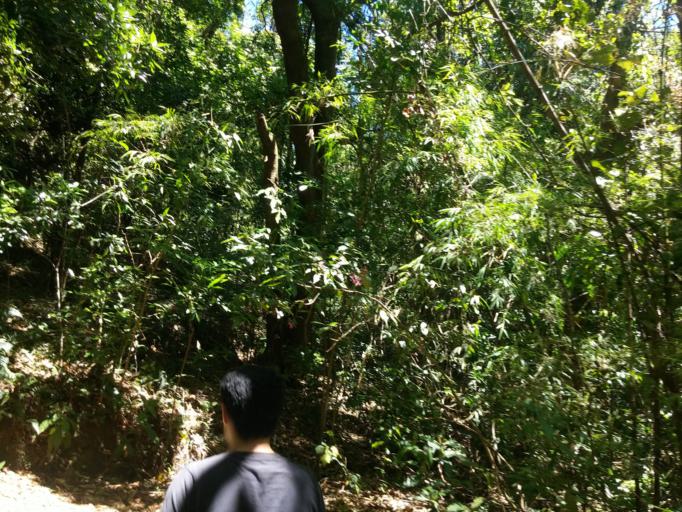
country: CR
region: Alajuela
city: Sabanilla
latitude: 10.1452
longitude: -84.2448
